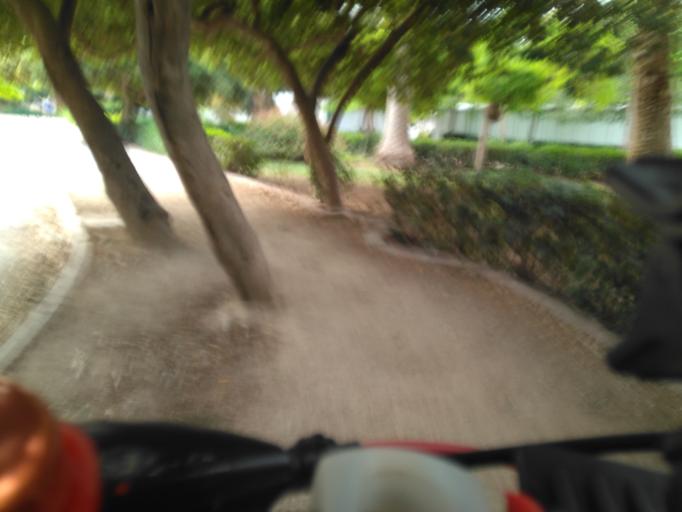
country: ES
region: Valencia
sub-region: Provincia de Valencia
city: Valencia
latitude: 39.4799
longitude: -0.3680
